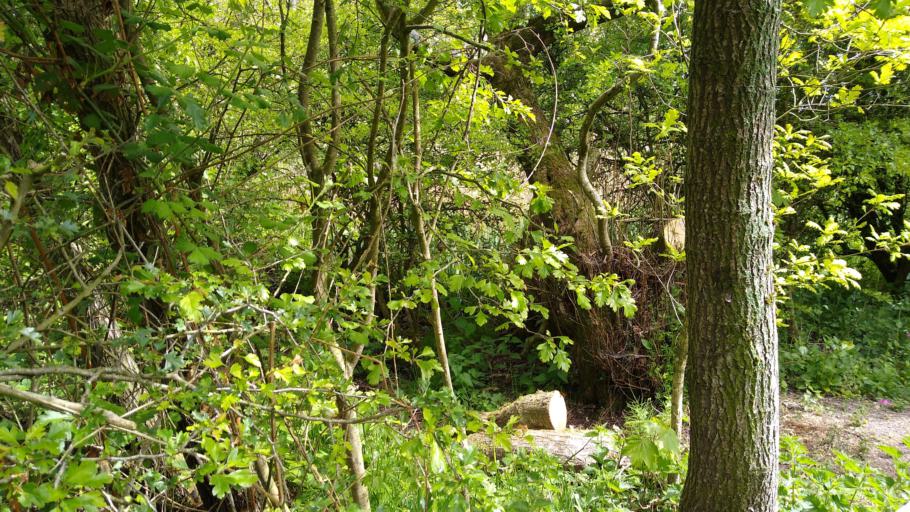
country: GB
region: England
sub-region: Cumbria
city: Dearham
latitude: 54.7422
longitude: -3.4537
